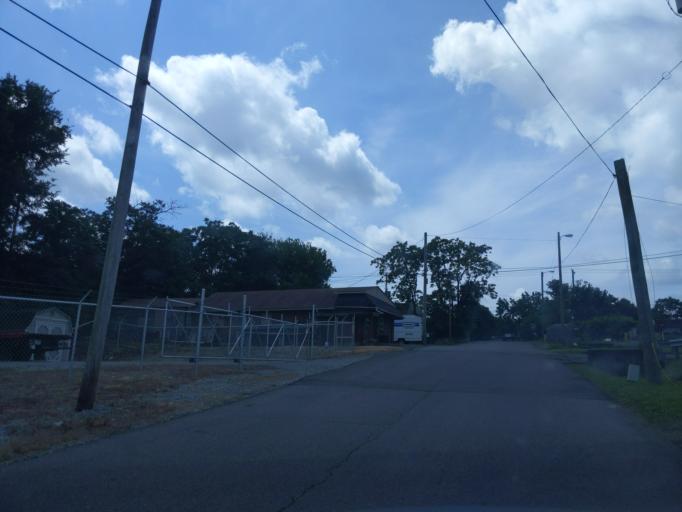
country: US
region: Tennessee
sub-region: Davidson County
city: Nashville
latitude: 36.1543
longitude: -86.7502
